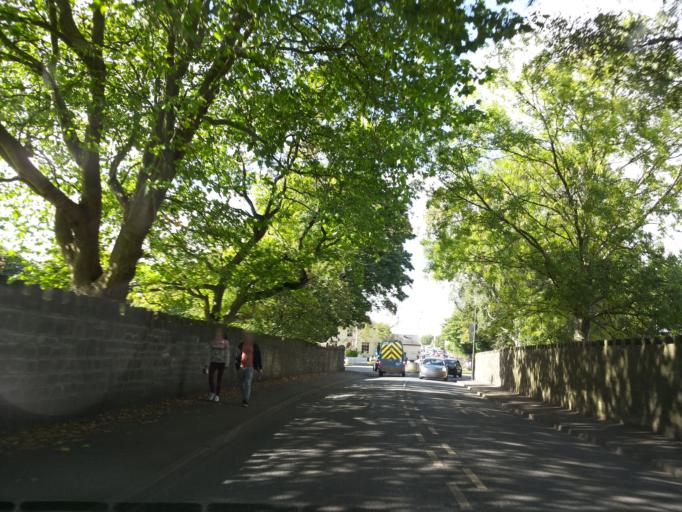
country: GB
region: England
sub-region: Bath and North East Somerset
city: Bath
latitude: 51.3581
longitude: -2.3748
